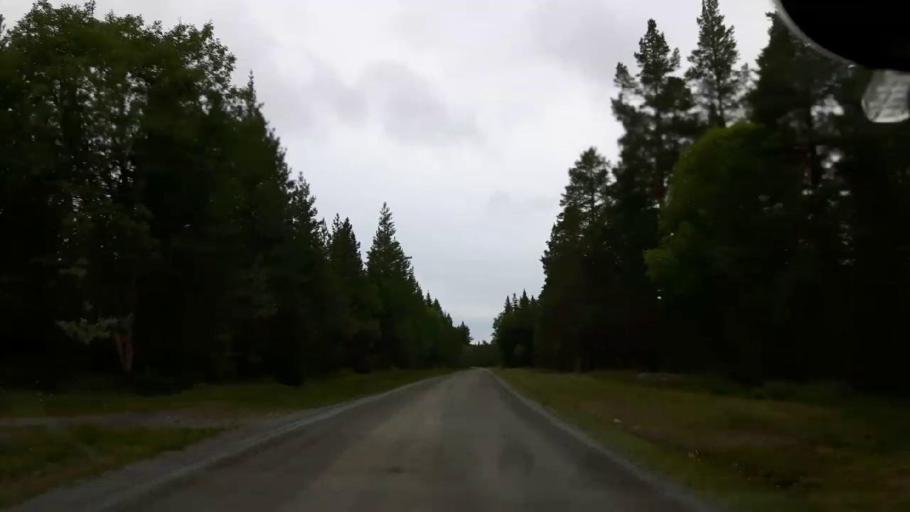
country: SE
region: Jaemtland
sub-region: OEstersunds Kommun
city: Ostersund
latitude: 63.1211
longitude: 14.5391
